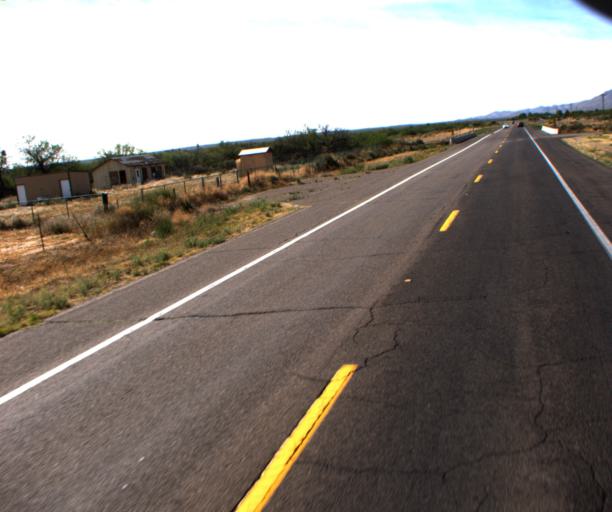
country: US
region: Arizona
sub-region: Graham County
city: Swift Trail Junction
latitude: 32.6947
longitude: -109.7078
